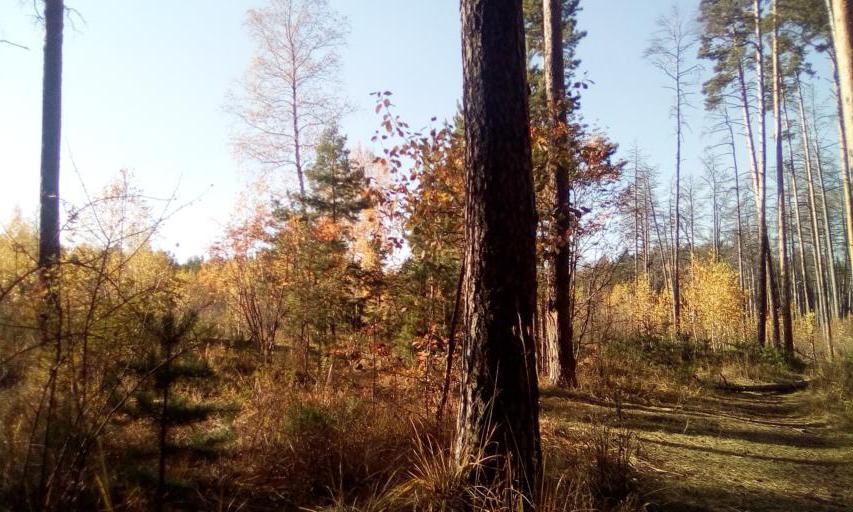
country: RU
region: Chelyabinsk
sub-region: Gorod Chelyabinsk
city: Chelyabinsk
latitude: 55.1621
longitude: 61.3559
